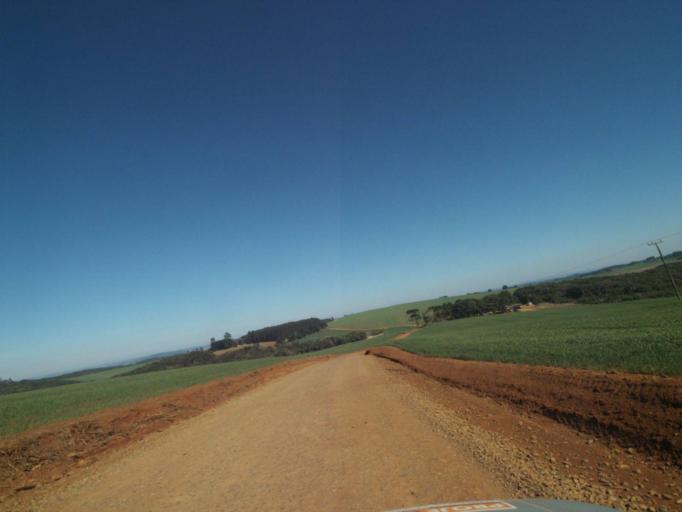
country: BR
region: Parana
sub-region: Tibagi
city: Tibagi
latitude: -24.6044
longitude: -50.6036
